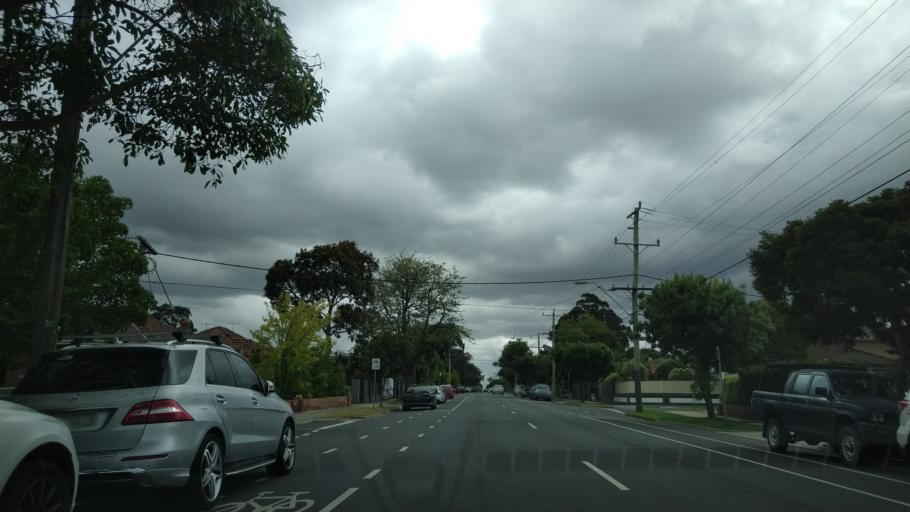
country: AU
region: Victoria
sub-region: Glen Eira
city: Caulfield South
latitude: -37.8974
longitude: 145.0269
